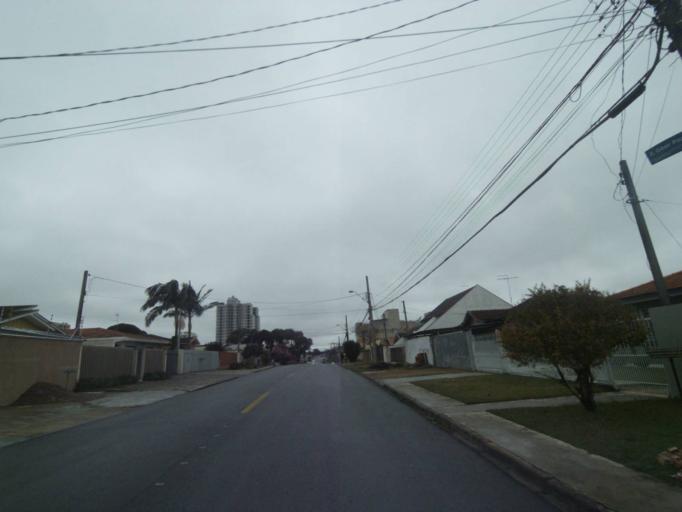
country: BR
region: Parana
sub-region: Curitiba
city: Curitiba
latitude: -25.5033
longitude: -49.3008
